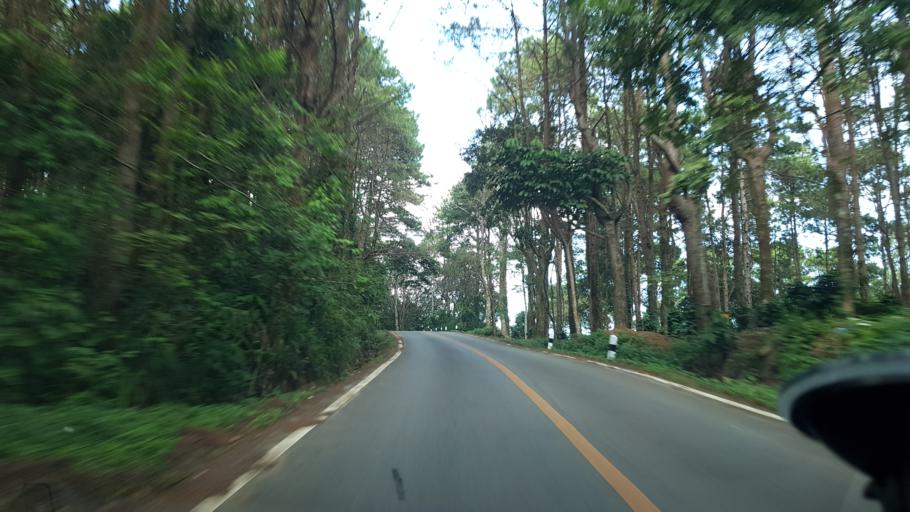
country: TH
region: Chiang Rai
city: Mae Fa Luang
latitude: 20.3303
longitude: 99.8152
